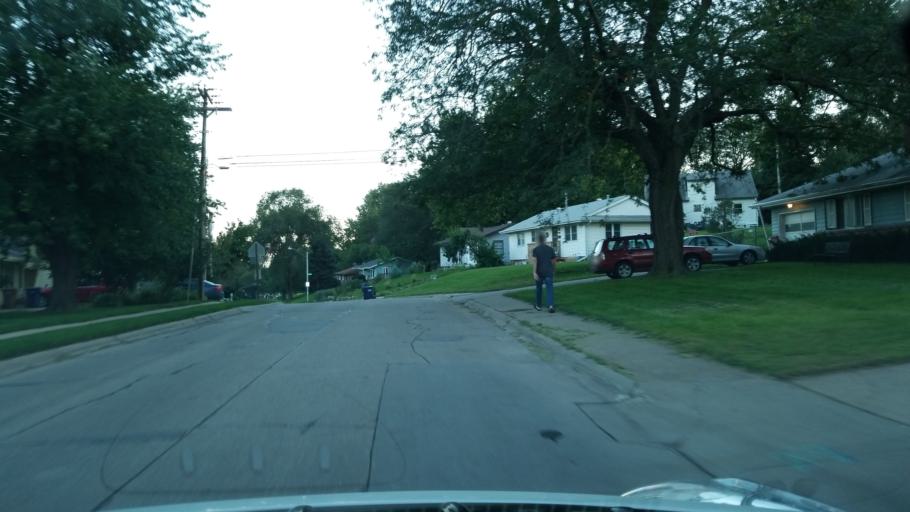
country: US
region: Nebraska
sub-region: Sarpy County
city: Bellevue
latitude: 41.1451
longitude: -95.9017
